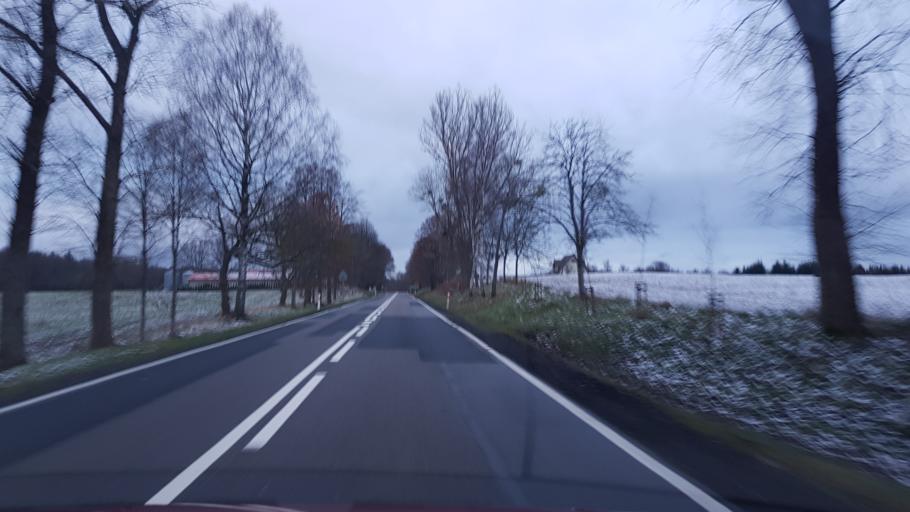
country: PL
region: Pomeranian Voivodeship
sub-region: Powiat bytowski
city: Tuchomie
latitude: 54.0880
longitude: 17.3062
